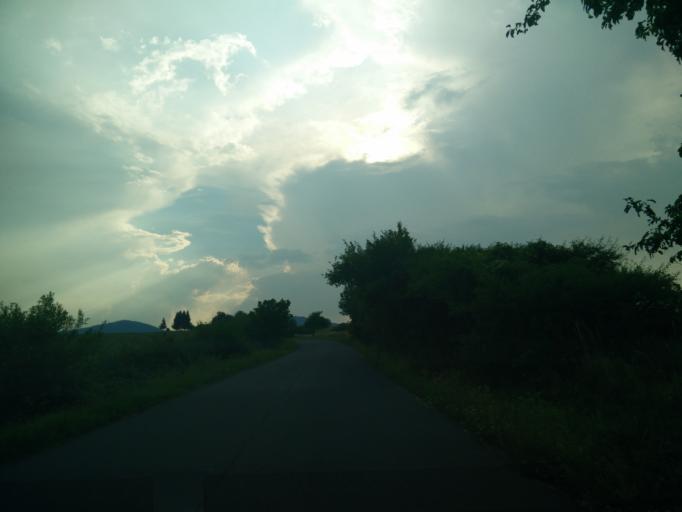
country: SK
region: Banskobystricky
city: Ziar nad Hronom
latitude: 48.6515
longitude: 18.8033
